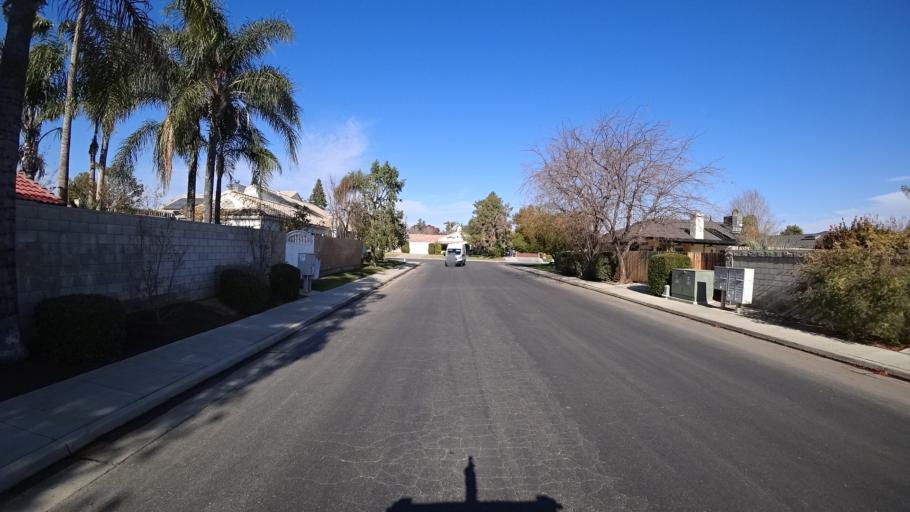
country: US
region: California
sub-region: Kern County
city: Greenacres
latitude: 35.4041
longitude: -119.0854
